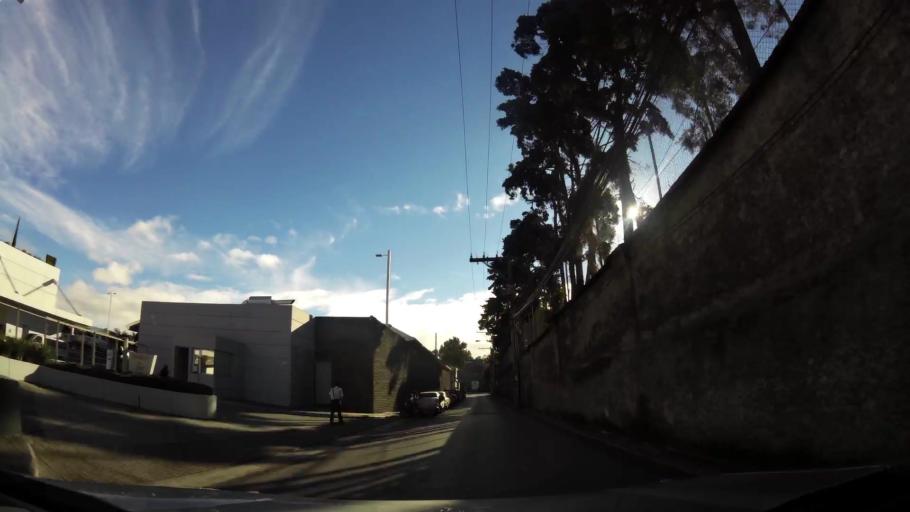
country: GT
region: Guatemala
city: Guatemala City
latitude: 14.6175
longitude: -90.5122
